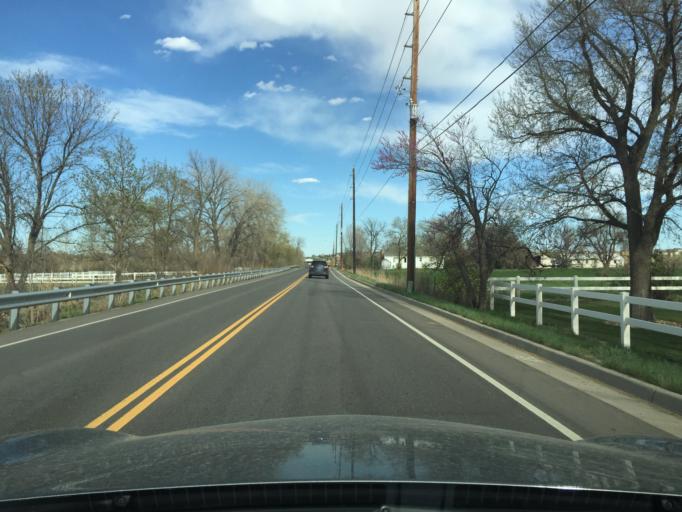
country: US
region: Colorado
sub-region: Boulder County
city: Lafayette
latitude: 40.0365
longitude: -105.0965
